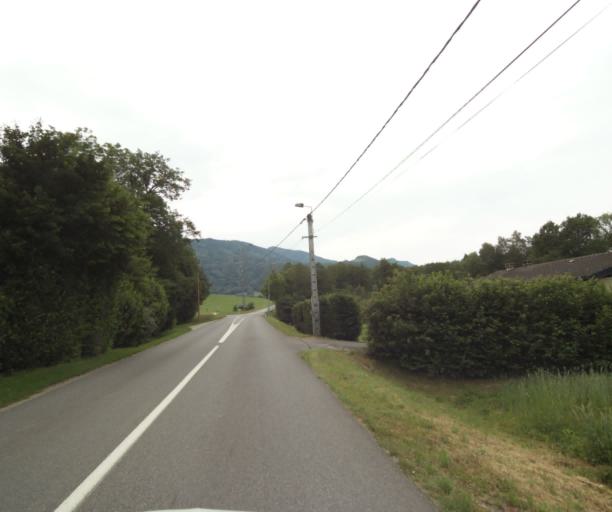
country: FR
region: Rhone-Alpes
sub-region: Departement de la Haute-Savoie
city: Allinges
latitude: 46.3215
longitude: 6.4747
